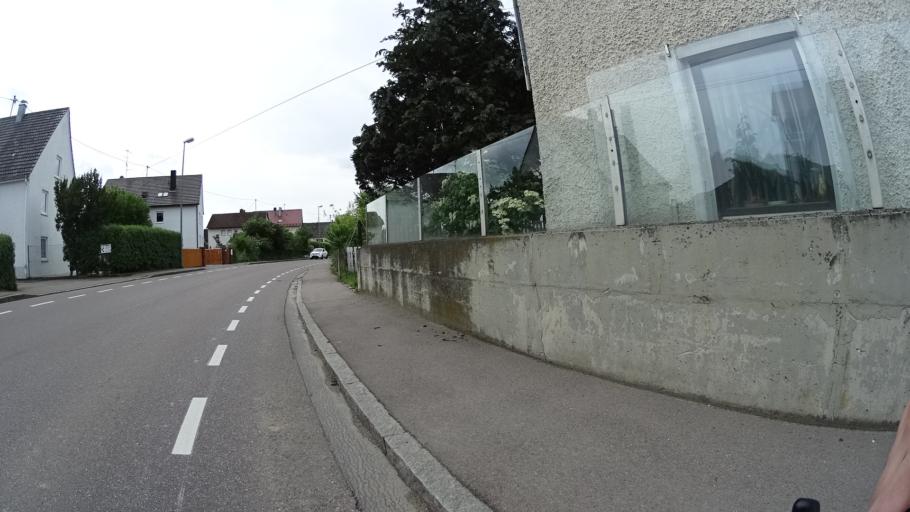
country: DE
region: Bavaria
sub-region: Swabia
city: Weissenhorn
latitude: 48.3294
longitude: 10.1617
